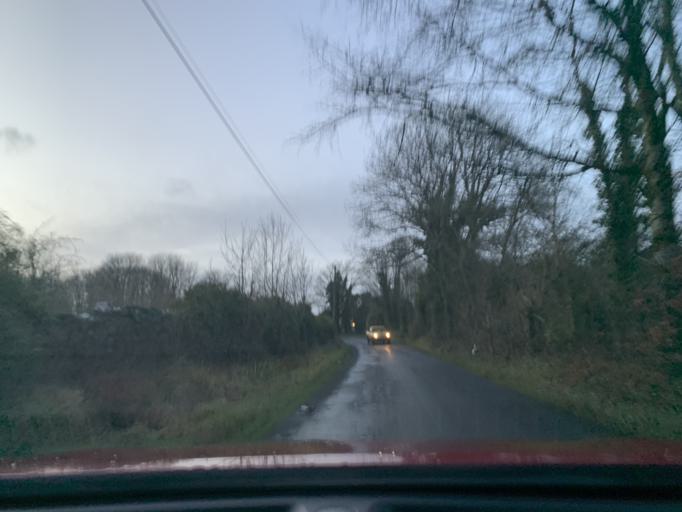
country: IE
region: Connaught
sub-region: Sligo
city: Ballymote
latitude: 54.1231
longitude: -8.5821
